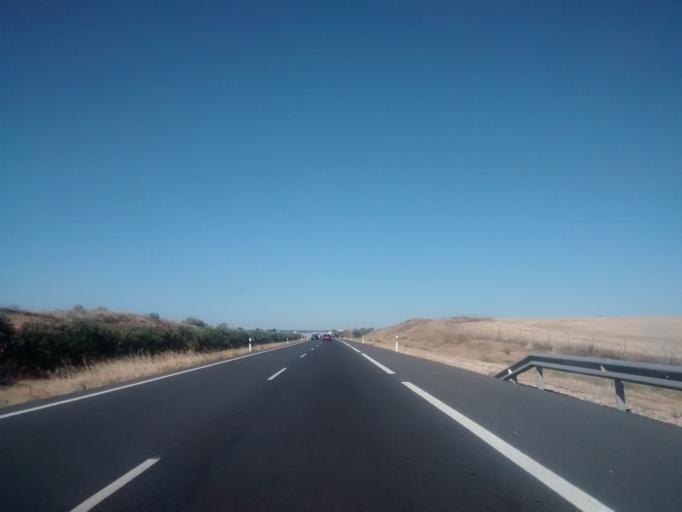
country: ES
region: Andalusia
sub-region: Provincia de Huelva
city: Aljaraque
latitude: 37.3316
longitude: -7.0391
